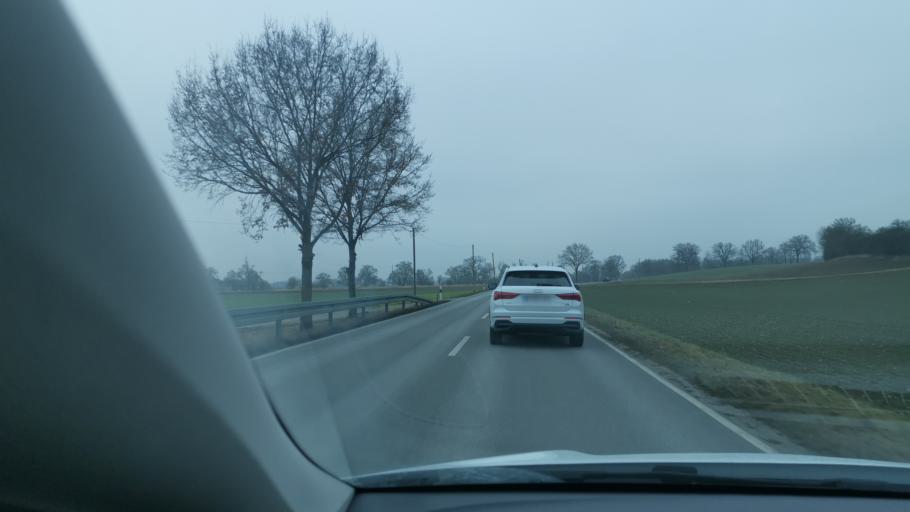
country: DE
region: Bavaria
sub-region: Swabia
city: Thierhaupten
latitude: 48.5507
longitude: 10.9098
